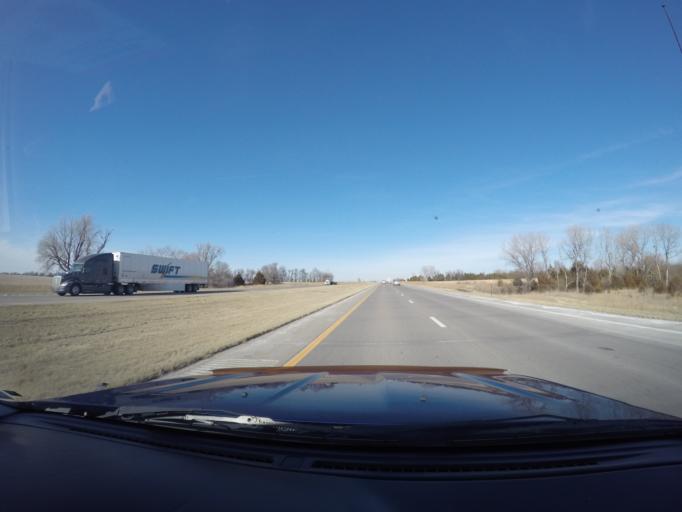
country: US
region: Kansas
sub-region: Sedgwick County
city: Valley Center
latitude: 37.9171
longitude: -97.3269
